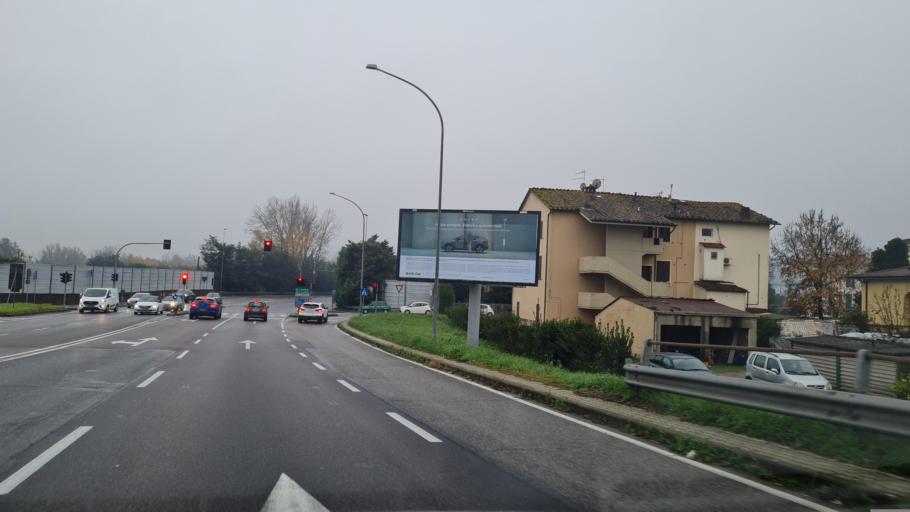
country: IT
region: Tuscany
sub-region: Provincia di Lucca
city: Lucca
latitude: 43.8373
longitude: 10.4763
